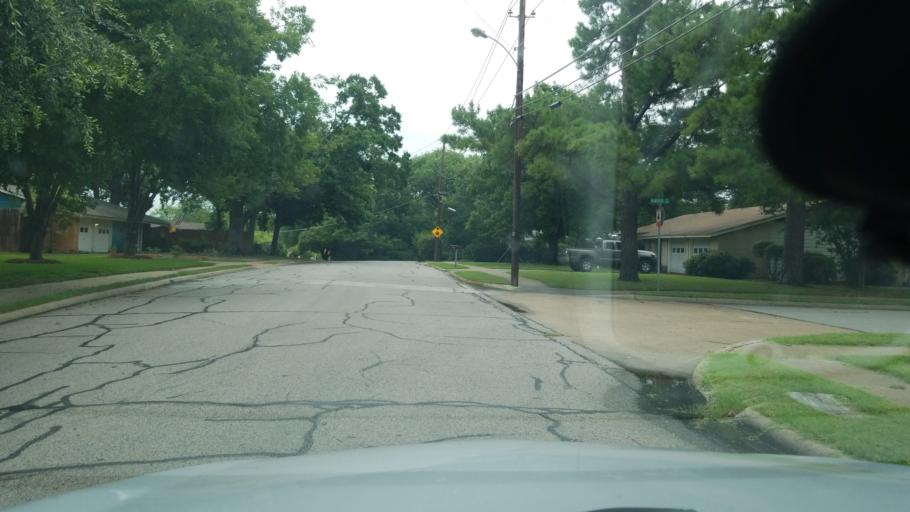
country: US
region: Texas
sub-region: Dallas County
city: Irving
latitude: 32.8520
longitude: -96.9472
